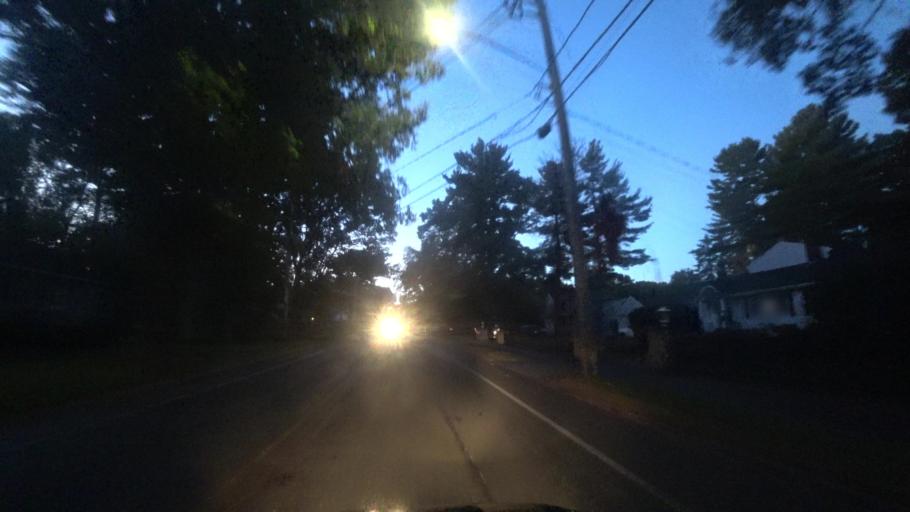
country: US
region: Massachusetts
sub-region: Middlesex County
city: Reading
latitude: 42.5342
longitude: -71.0849
